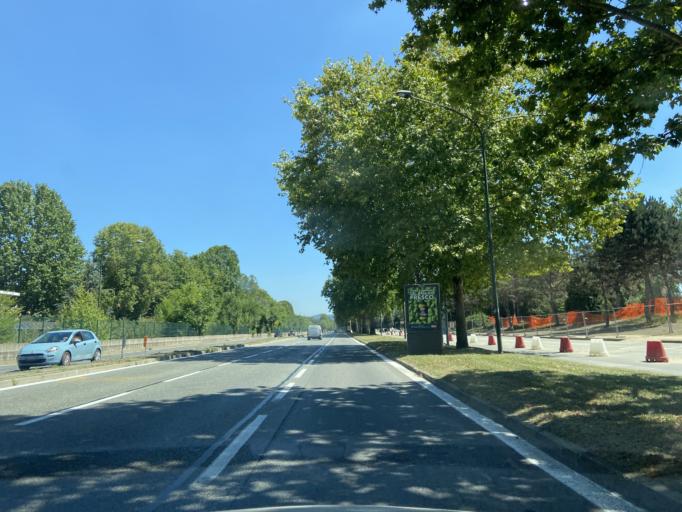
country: IT
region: Piedmont
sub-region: Provincia di Torino
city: Savonera
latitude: 45.0918
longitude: 7.6379
